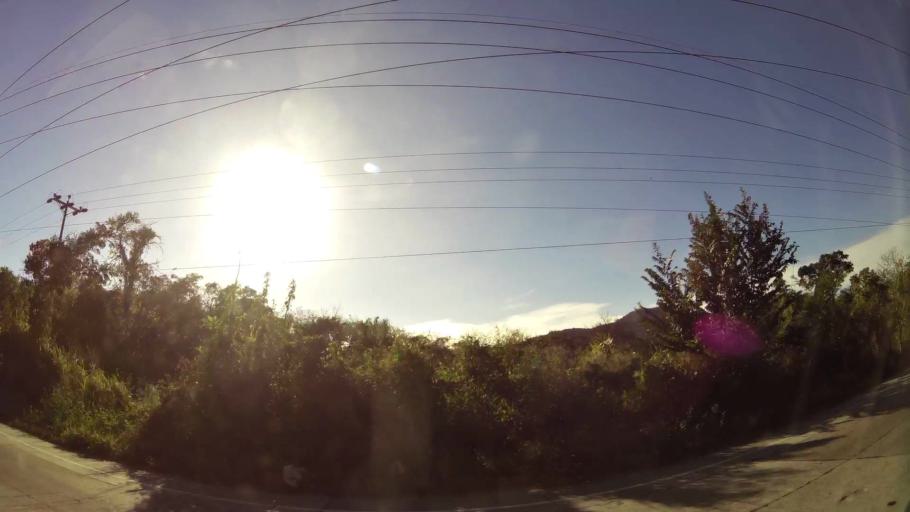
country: SV
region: Santa Ana
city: Metapan
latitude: 14.2662
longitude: -89.4602
